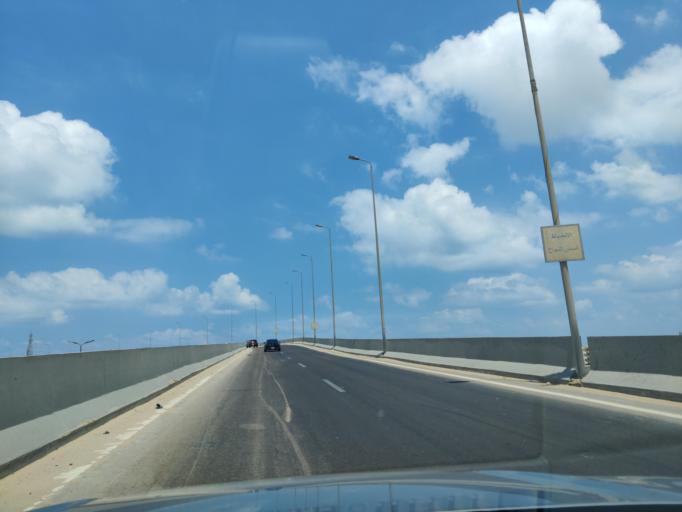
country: EG
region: Alexandria
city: Alexandria
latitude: 31.0126
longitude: 29.6345
